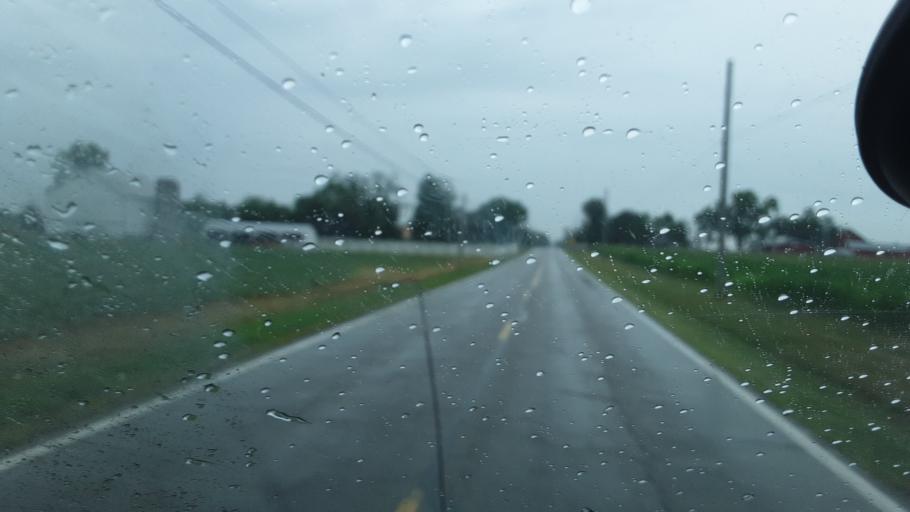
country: US
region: Ohio
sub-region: Williams County
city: Montpelier
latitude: 41.5539
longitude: -84.6131
